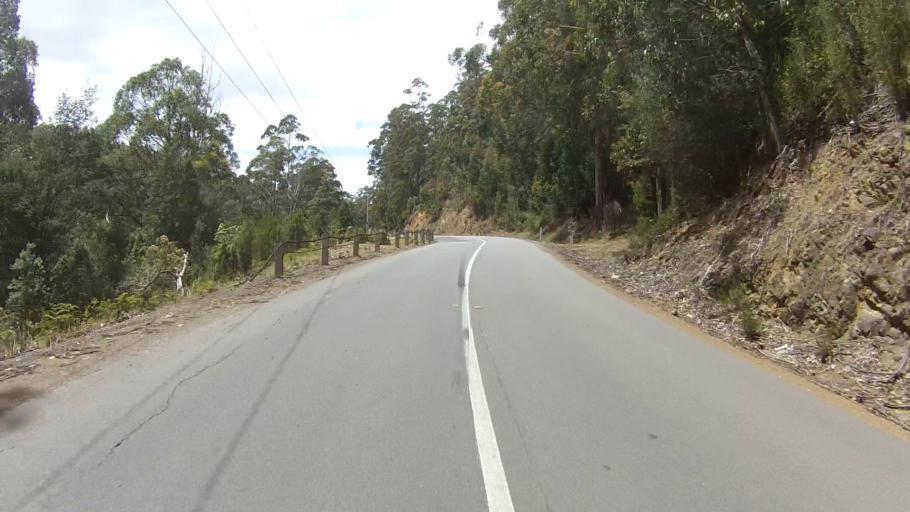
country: AU
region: Tasmania
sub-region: Kingborough
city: Kettering
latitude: -43.1259
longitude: 147.1732
